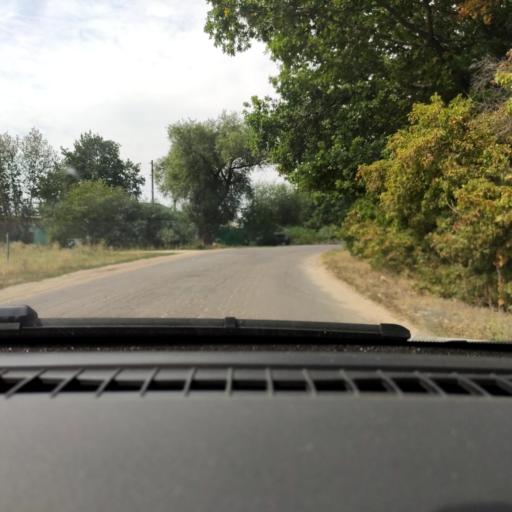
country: RU
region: Voronezj
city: Pridonskoy
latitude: 51.7384
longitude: 39.0565
